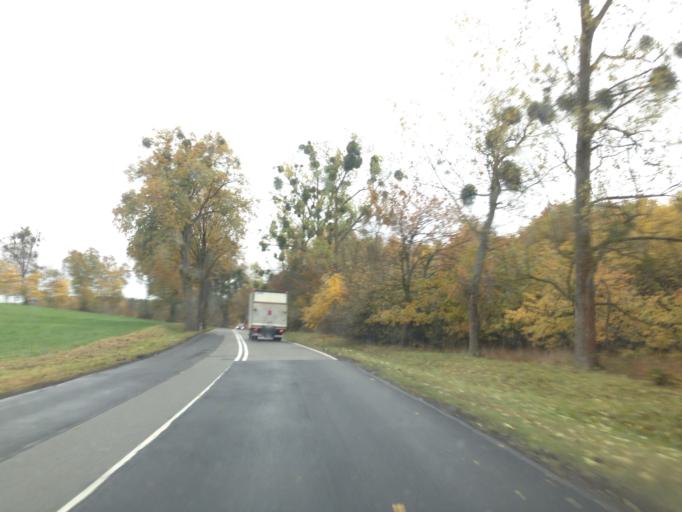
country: PL
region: Pomeranian Voivodeship
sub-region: Powiat kwidzynski
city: Ryjewo
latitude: 53.8500
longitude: 18.9987
